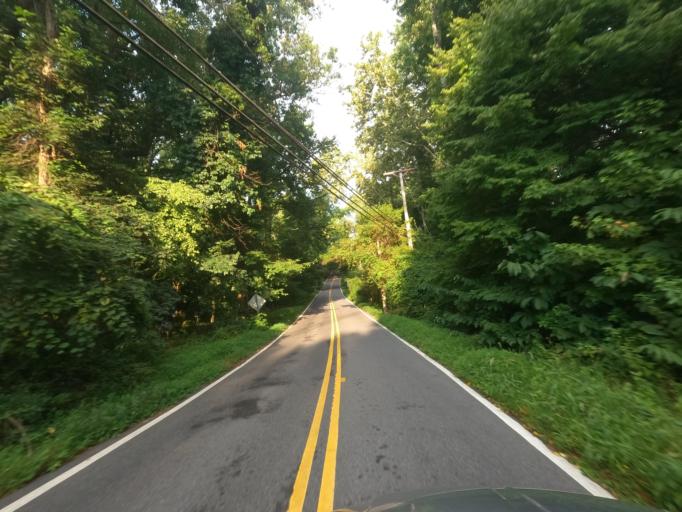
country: US
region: Maryland
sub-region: Prince George's County
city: Fort Washington
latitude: 38.6869
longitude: -77.0084
